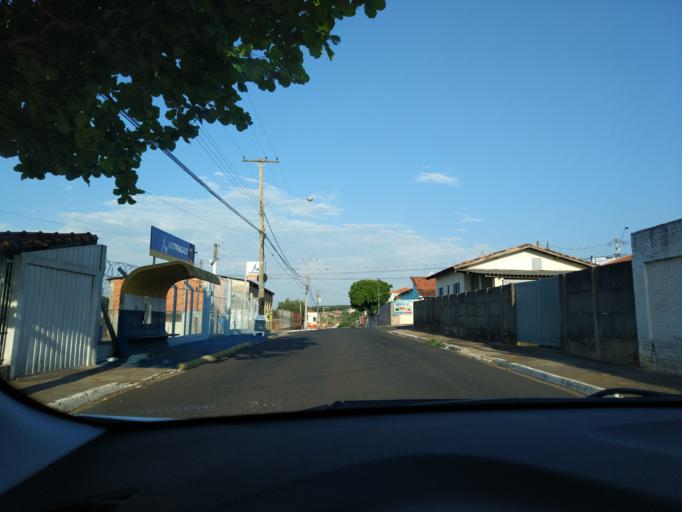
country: BR
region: Sao Paulo
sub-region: Botucatu
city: Botucatu
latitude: -22.8983
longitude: -48.4353
